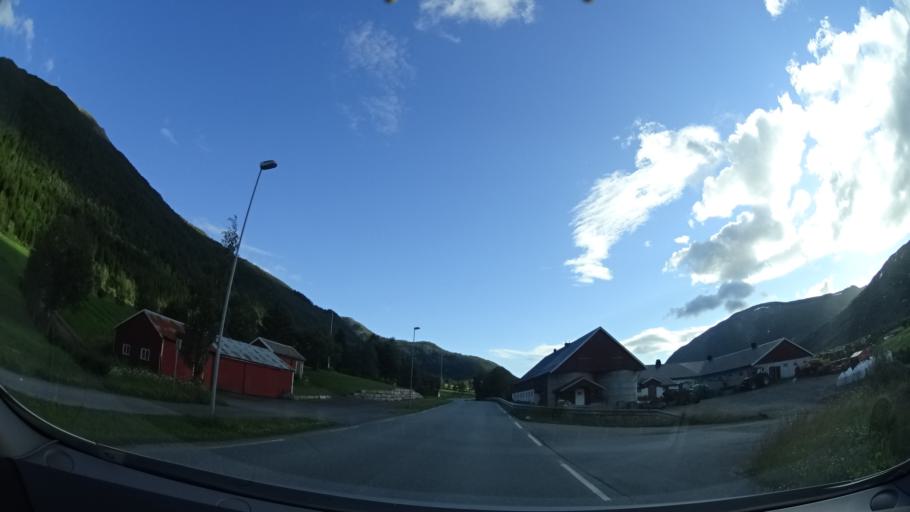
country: NO
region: More og Romsdal
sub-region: Gjemnes
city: Batnfjordsora
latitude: 62.8865
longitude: 7.6722
